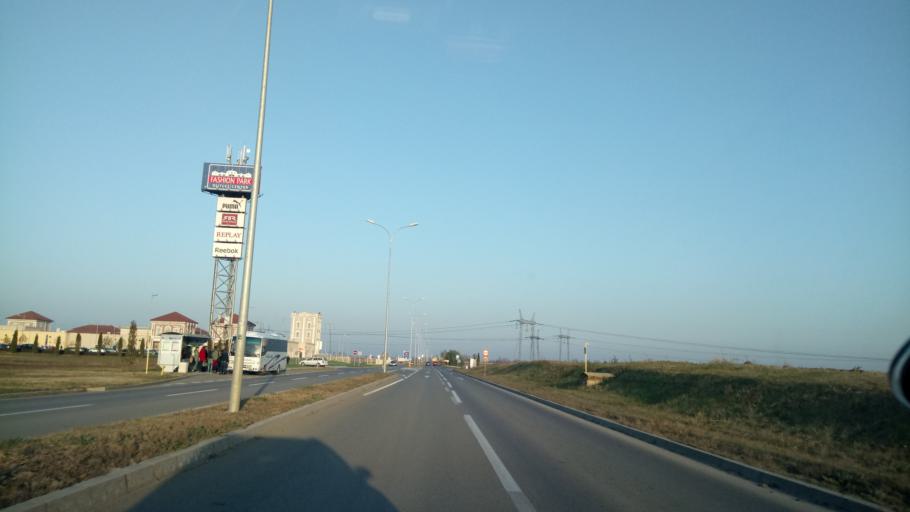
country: RS
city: Novi Karlovci
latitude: 45.0665
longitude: 20.1347
